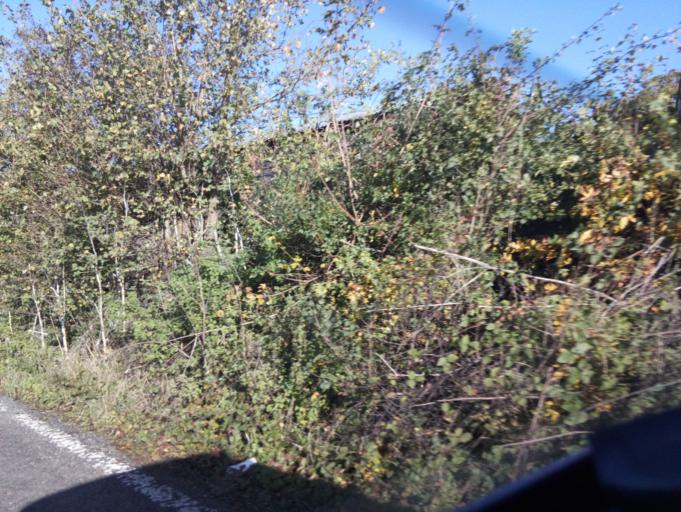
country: GB
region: England
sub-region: Somerset
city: Langport
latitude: 51.0525
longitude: -2.8392
